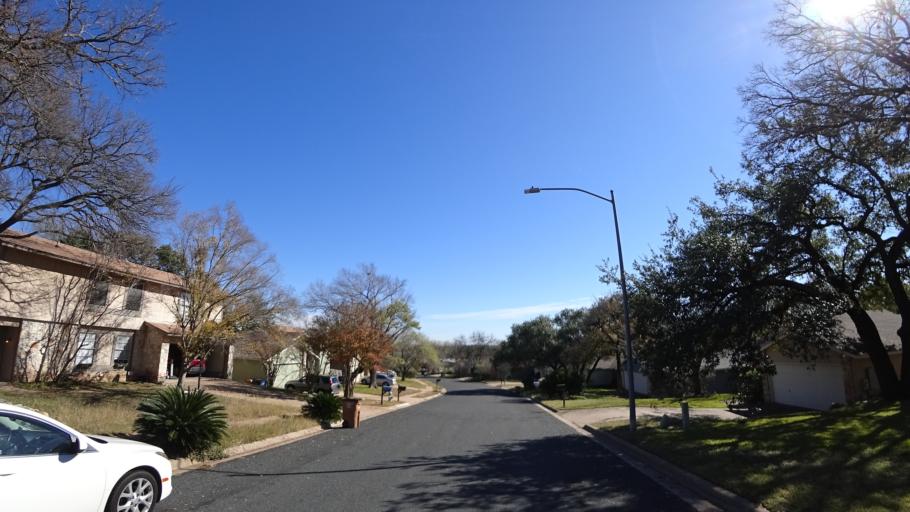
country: US
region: Texas
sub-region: Travis County
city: Wells Branch
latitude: 30.4182
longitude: -97.7155
